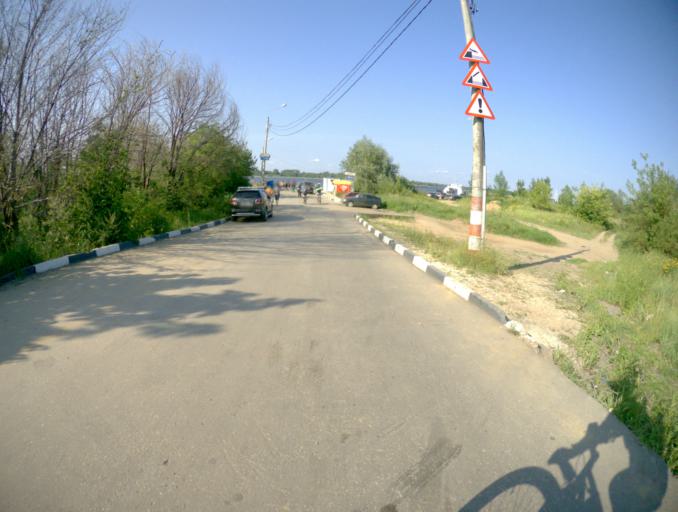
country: RU
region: Nizjnij Novgorod
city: Nizhniy Novgorod
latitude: 56.3312
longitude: 44.0230
